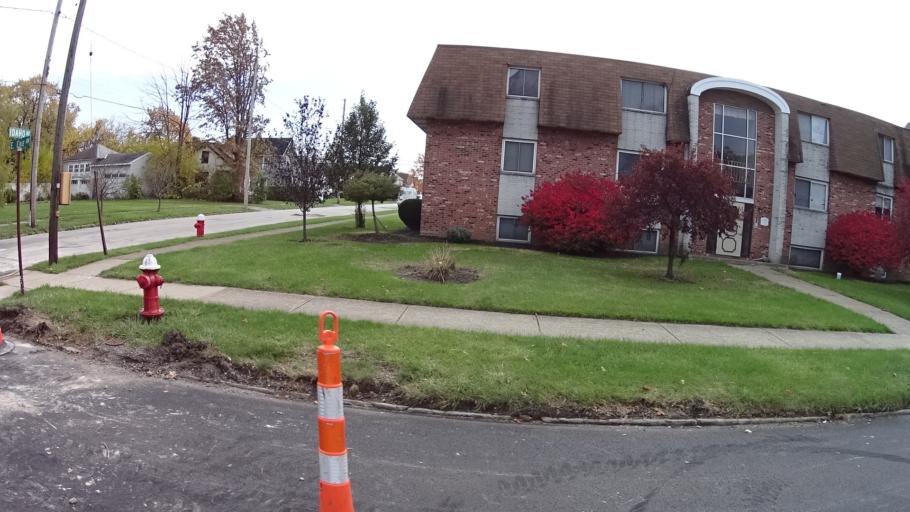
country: US
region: Ohio
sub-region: Lorain County
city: Lorain
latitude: 41.4737
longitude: -82.1646
